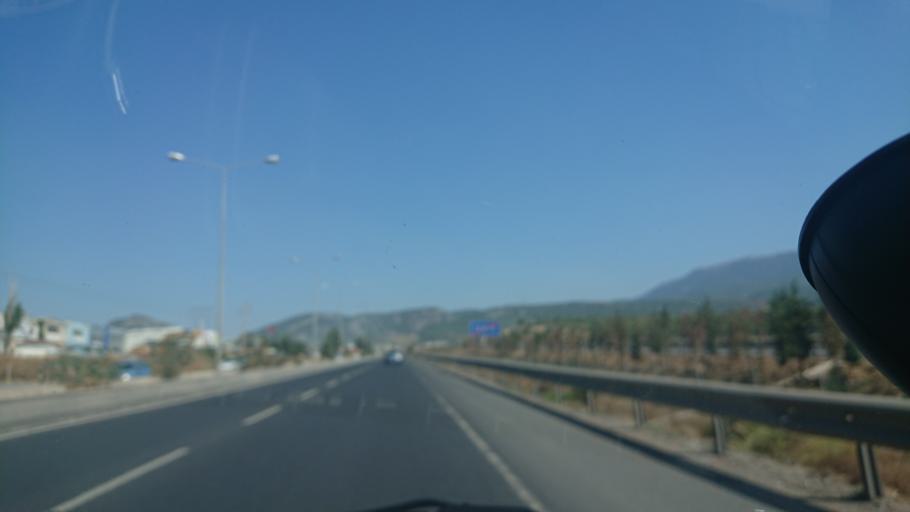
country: TR
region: Izmir
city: Bornova
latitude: 38.4508
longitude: 27.2762
